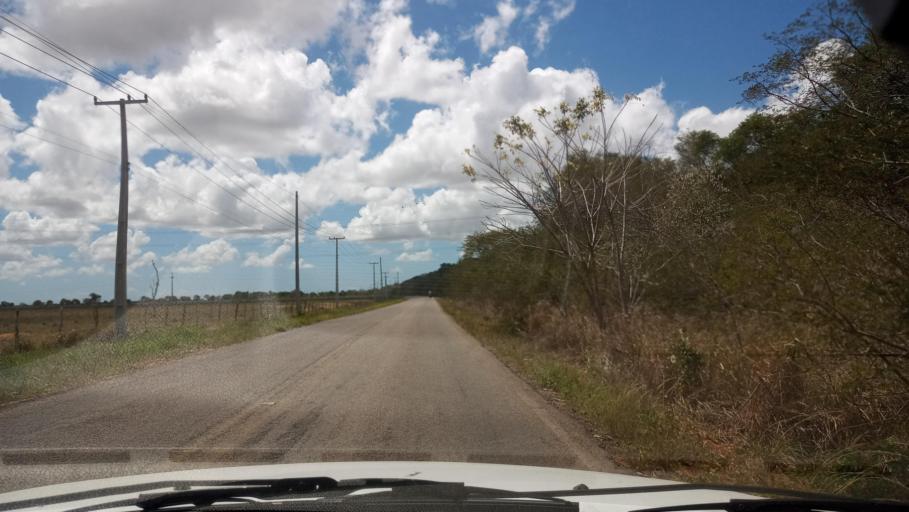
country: BR
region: Rio Grande do Norte
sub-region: Brejinho
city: Brejinho
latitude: -6.0408
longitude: -35.4146
